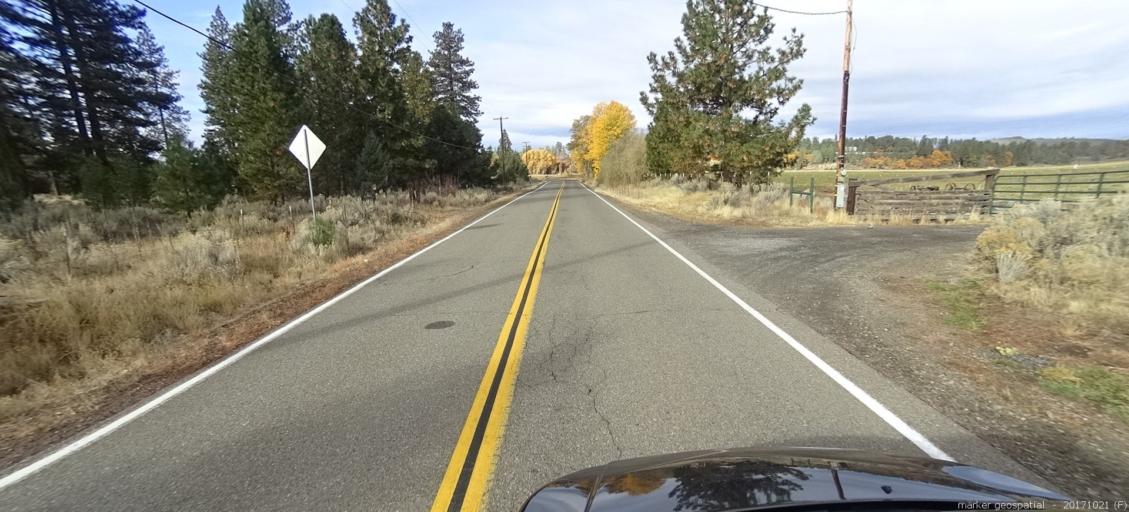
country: US
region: California
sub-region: Shasta County
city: Burney
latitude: 40.8991
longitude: -121.5490
